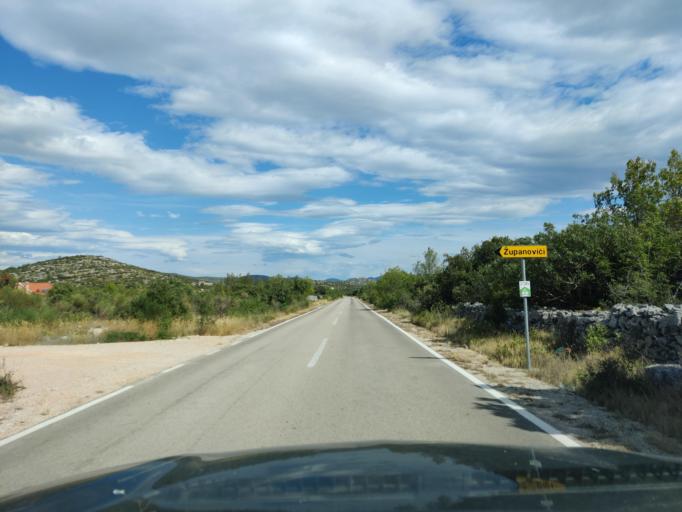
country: HR
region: Sibensko-Kniniska
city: Zaton
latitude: 43.7436
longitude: 15.8506
